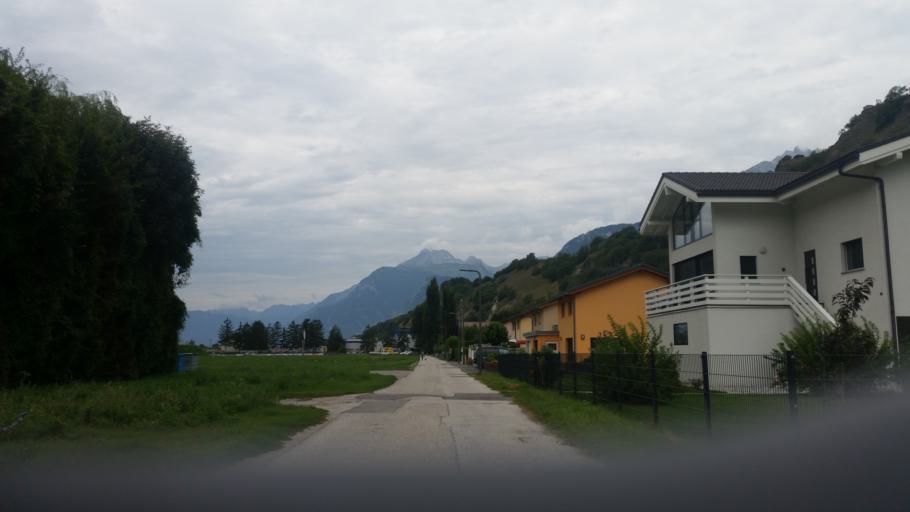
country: CH
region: Valais
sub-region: Conthey District
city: Conthey
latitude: 46.2221
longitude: 7.3241
